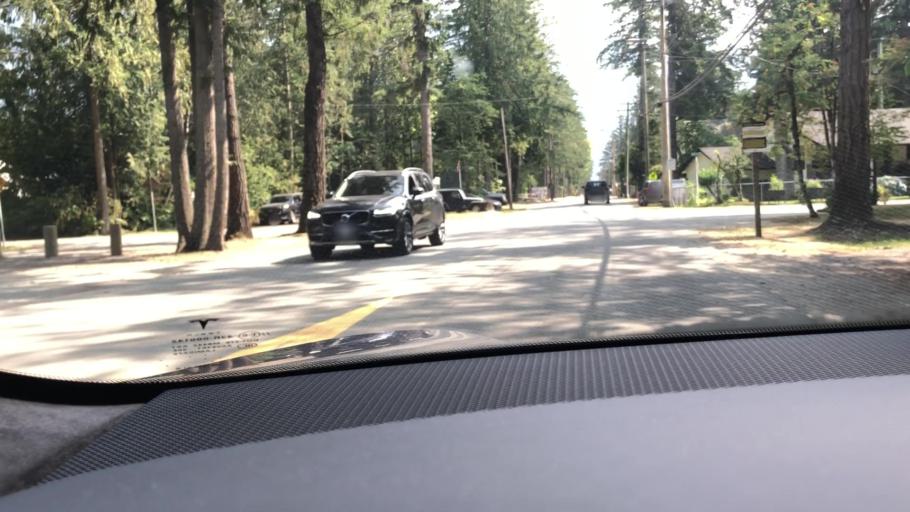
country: CA
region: British Columbia
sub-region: Fraser Valley Regional District
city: Chilliwack
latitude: 49.0739
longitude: -121.9763
